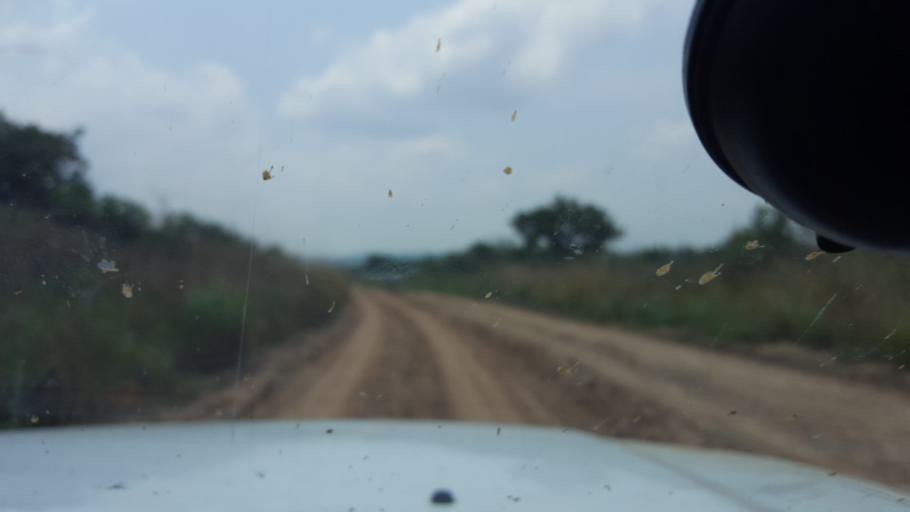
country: CD
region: Bandundu
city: Mushie
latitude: -3.7516
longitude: 16.6422
